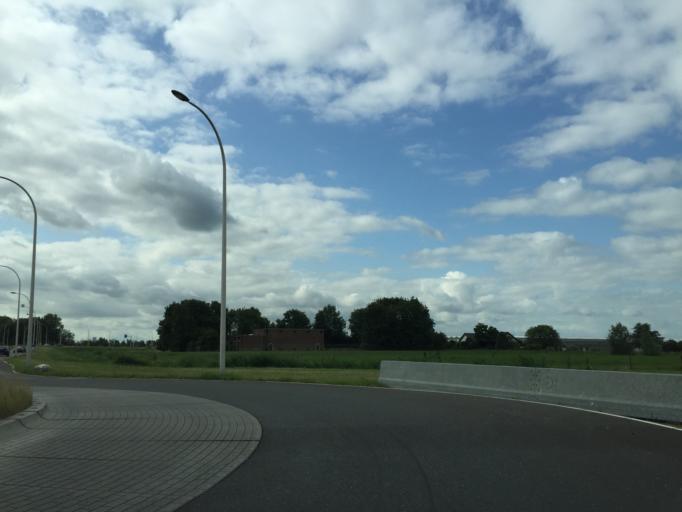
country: NL
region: South Holland
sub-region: Gemeente Pijnacker-Nootdorp
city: Pijnacker
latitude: 52.0090
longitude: 4.4296
